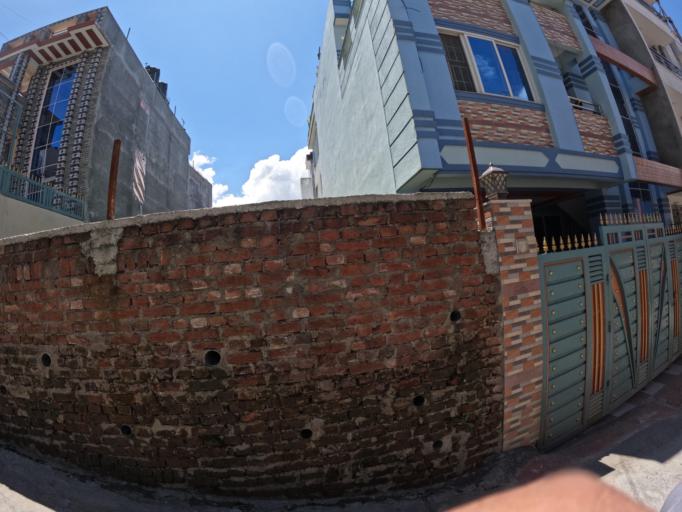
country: NP
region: Central Region
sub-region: Bagmati Zone
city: Kathmandu
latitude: 27.7518
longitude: 85.3274
